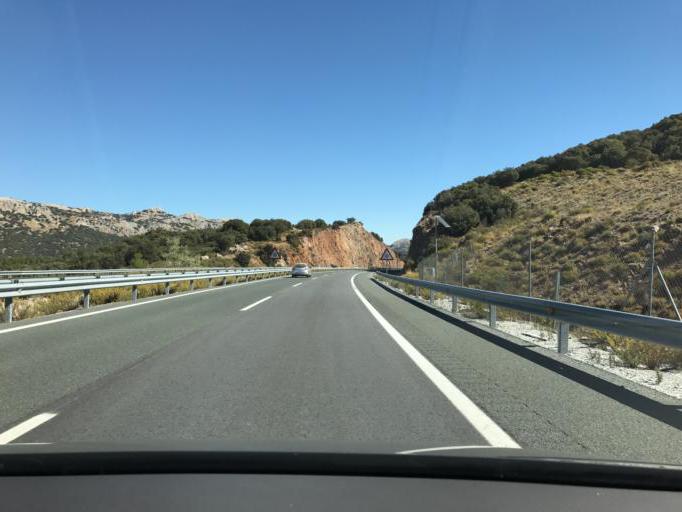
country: ES
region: Andalusia
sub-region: Provincia de Granada
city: Beas de Granada
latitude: 37.2980
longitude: -3.4470
